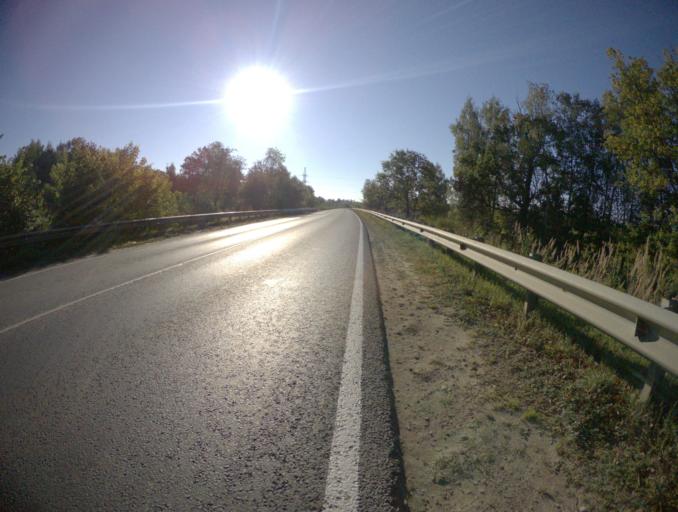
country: RU
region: Vladimir
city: Sobinka
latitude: 56.0036
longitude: 40.0067
